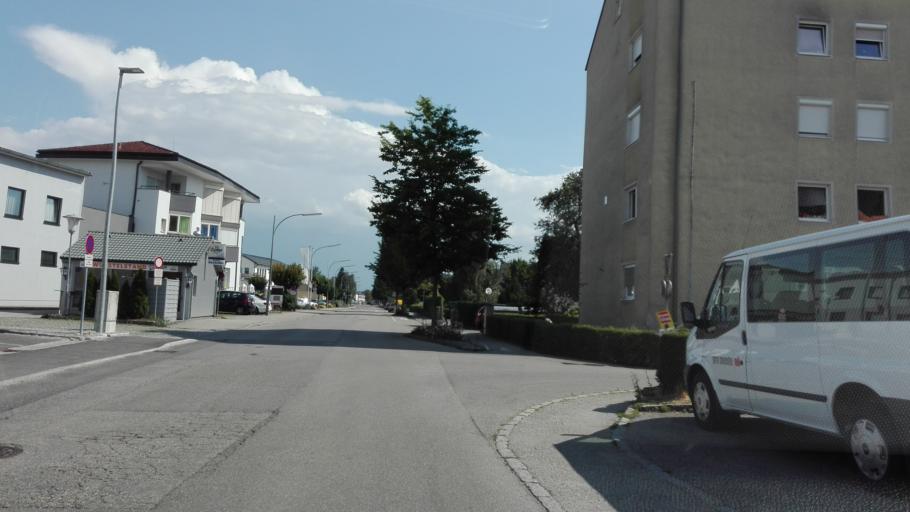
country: AT
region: Upper Austria
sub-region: Politischer Bezirk Perg
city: Perg
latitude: 48.2462
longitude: 14.6350
